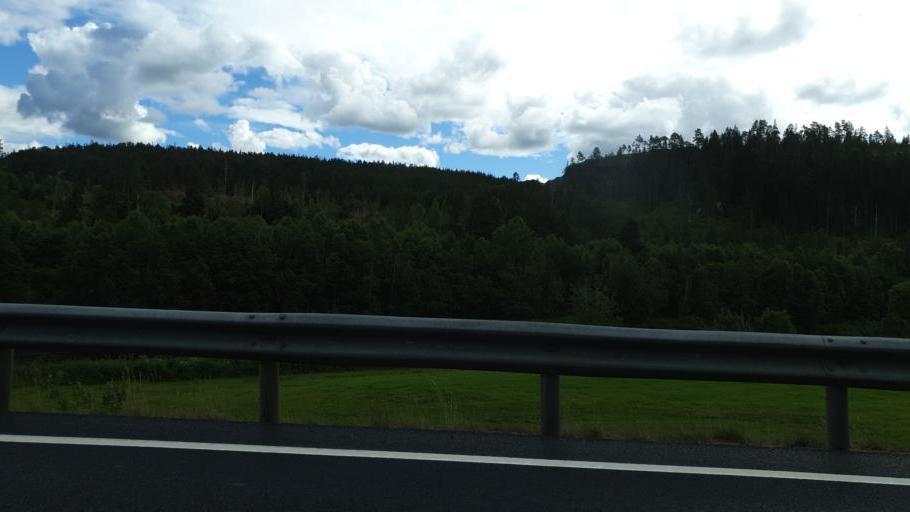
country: NO
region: Sor-Trondelag
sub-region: Rennebu
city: Berkak
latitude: 62.9198
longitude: 10.1446
